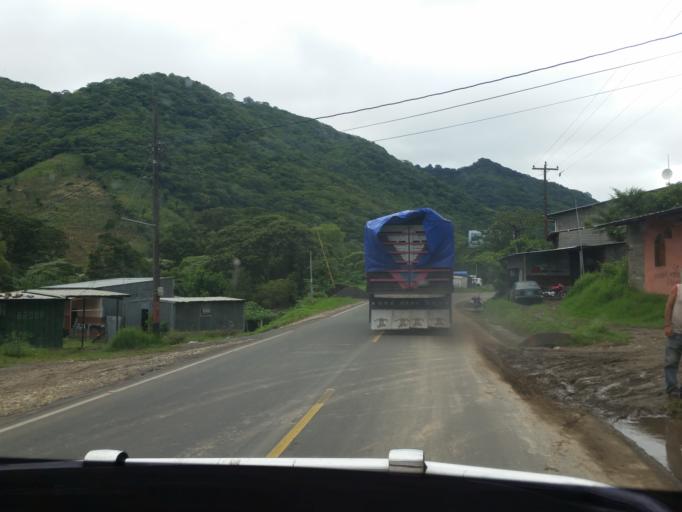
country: NI
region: Jinotega
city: Jinotega
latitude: 13.1047
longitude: -86.0021
